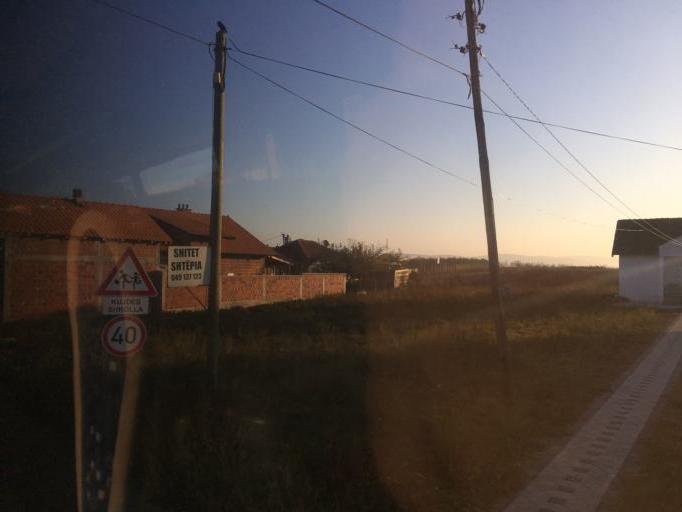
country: XK
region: Pristina
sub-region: Komuna e Drenasit
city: Glogovac
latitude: 42.5960
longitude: 20.8929
